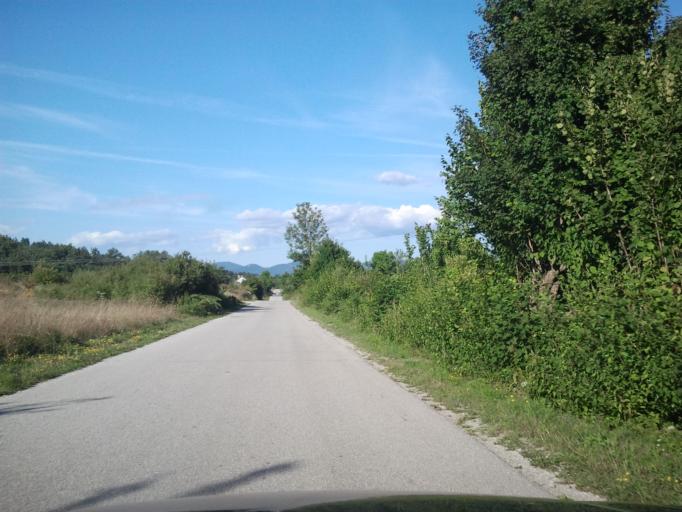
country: HR
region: Zadarska
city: Obrovac
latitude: 44.3529
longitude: 15.6452
